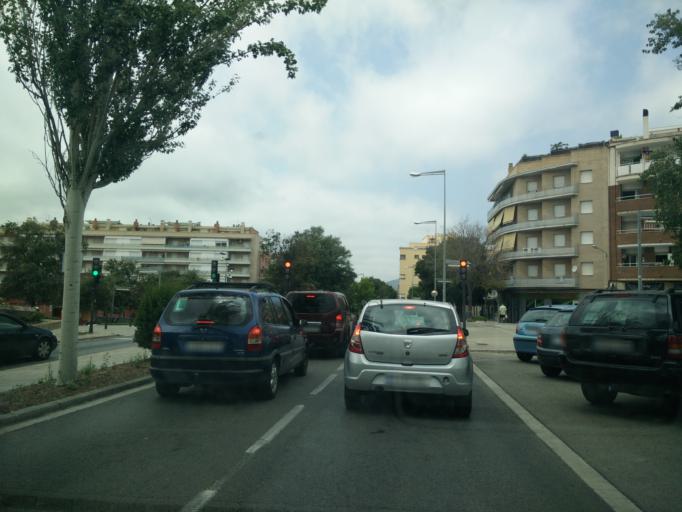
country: ES
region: Catalonia
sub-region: Provincia de Barcelona
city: Terrassa
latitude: 41.5692
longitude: 2.0240
